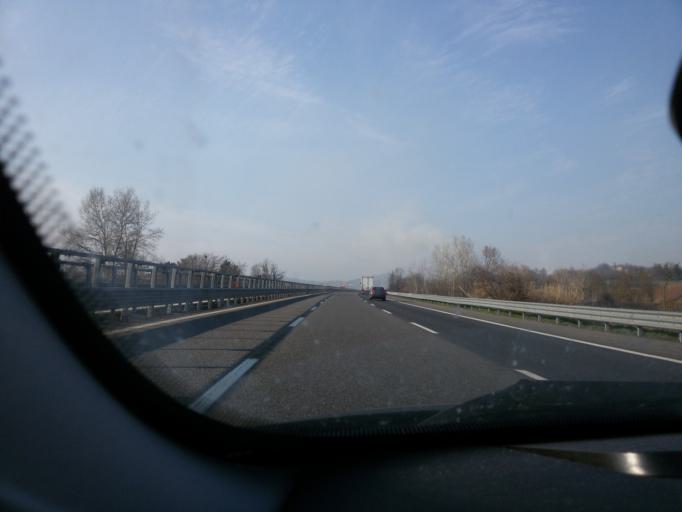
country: IT
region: Piedmont
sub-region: Provincia di Alessandria
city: Castelletto Monferrato
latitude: 44.9666
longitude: 8.5524
